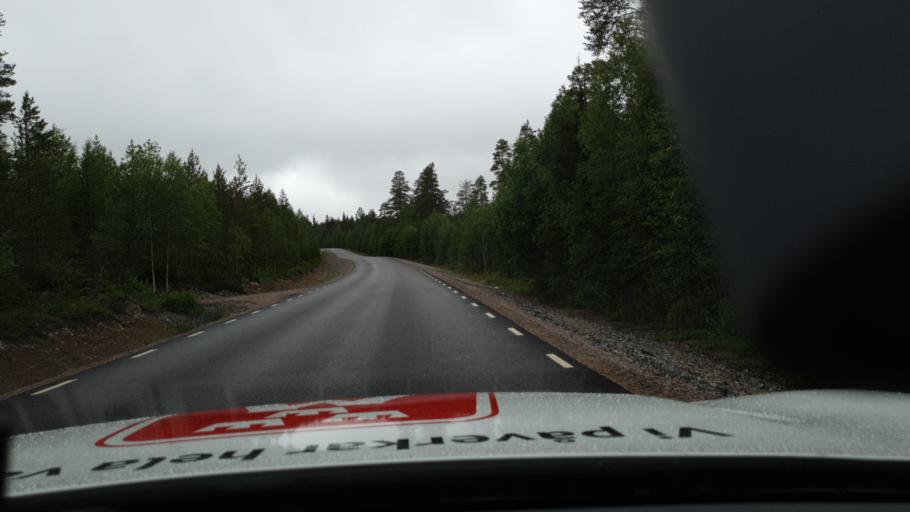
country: SE
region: Norrbotten
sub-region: Overtornea Kommun
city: OEvertornea
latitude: 66.4345
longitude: 23.5125
